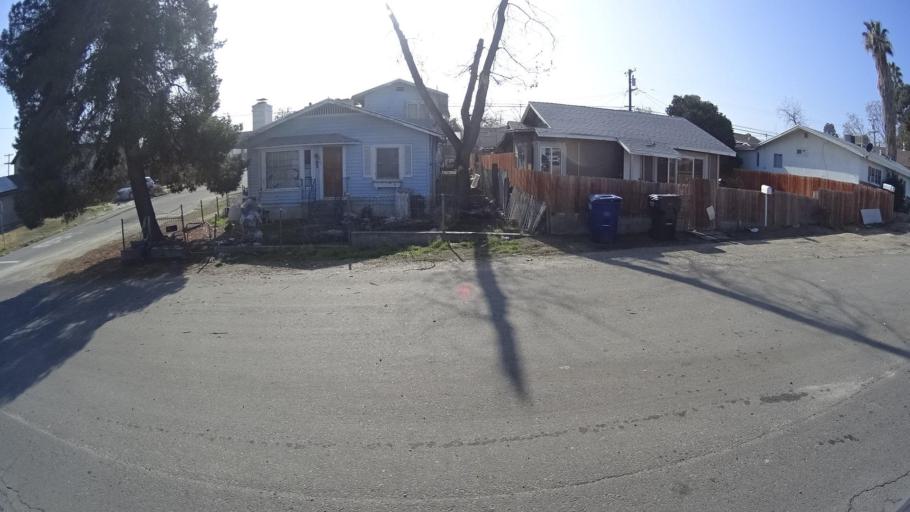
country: US
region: California
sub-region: Kern County
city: Taft Heights
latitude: 35.1368
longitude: -119.4676
